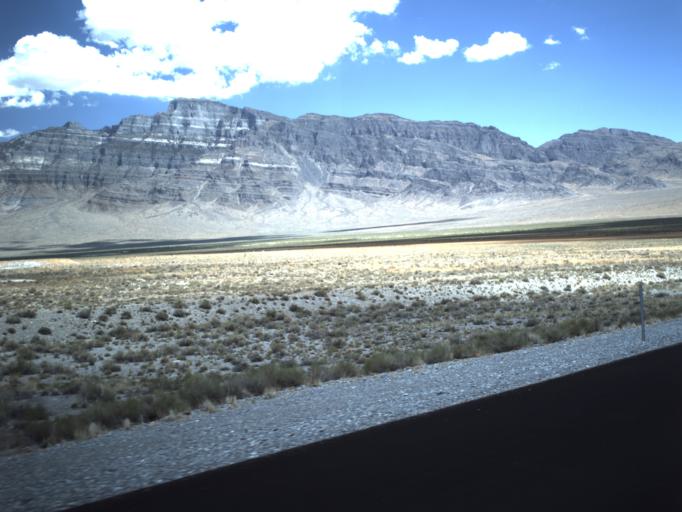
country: US
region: Utah
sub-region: Beaver County
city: Milford
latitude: 39.0836
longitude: -113.4990
